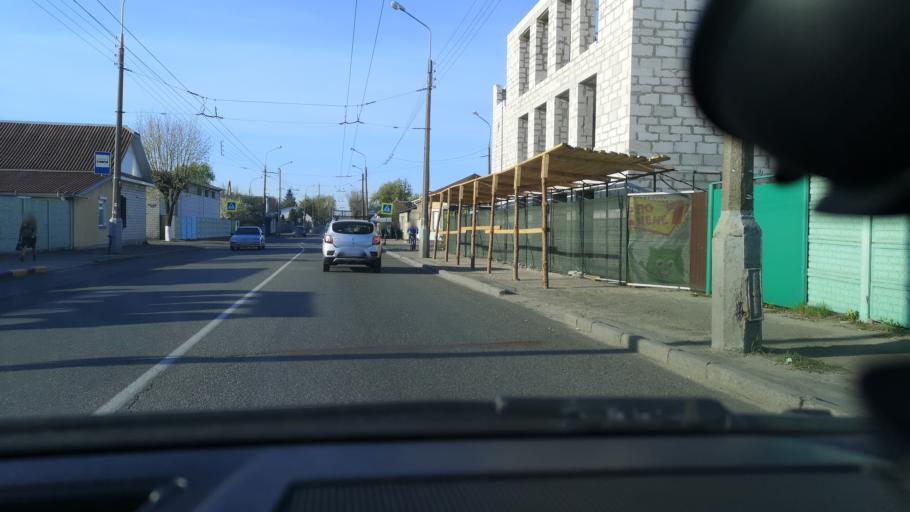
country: BY
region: Gomel
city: Gomel
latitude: 52.4380
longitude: 30.9774
